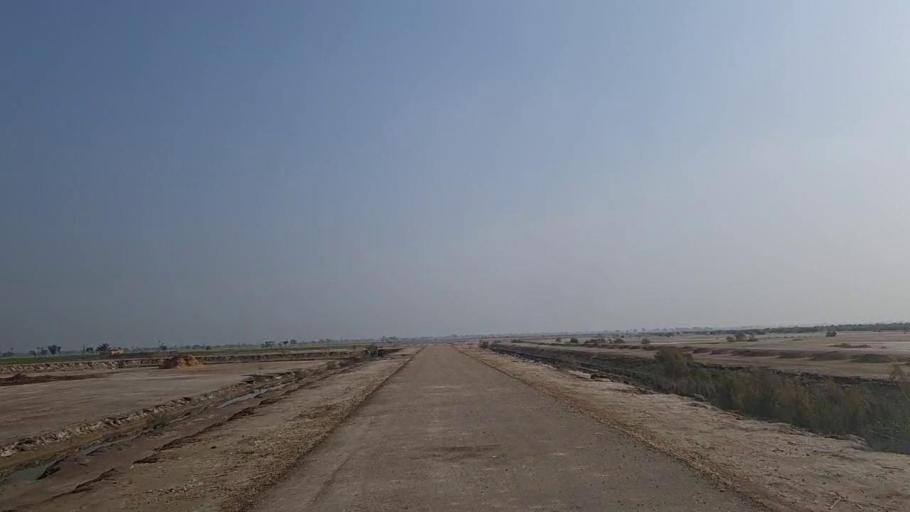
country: PK
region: Sindh
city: Nawabshah
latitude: 26.3459
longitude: 68.4534
